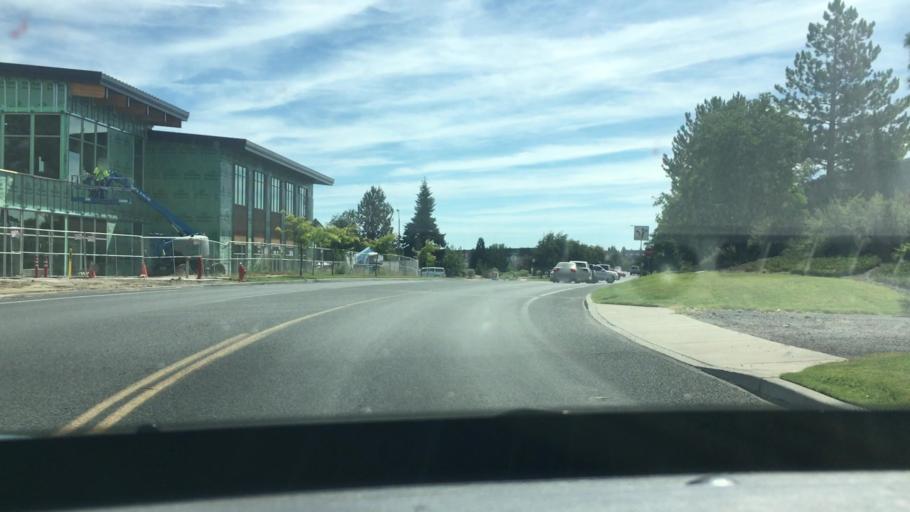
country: US
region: Oregon
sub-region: Deschutes County
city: Bend
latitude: 44.0483
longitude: -121.3283
